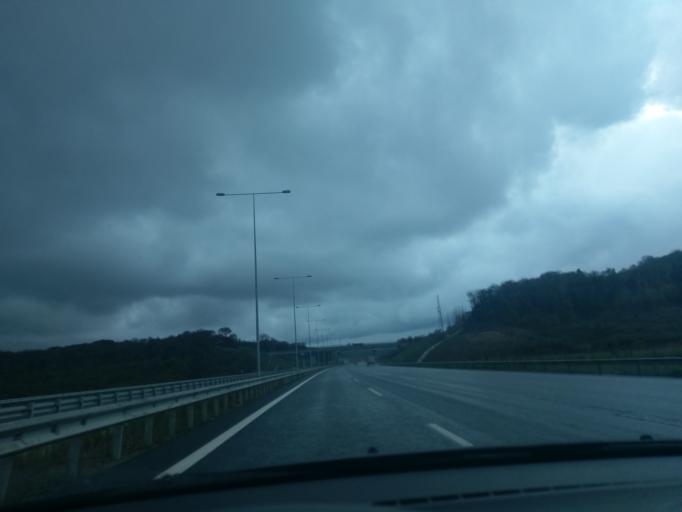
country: TR
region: Istanbul
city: Kemerburgaz
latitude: 41.2347
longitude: 28.9146
